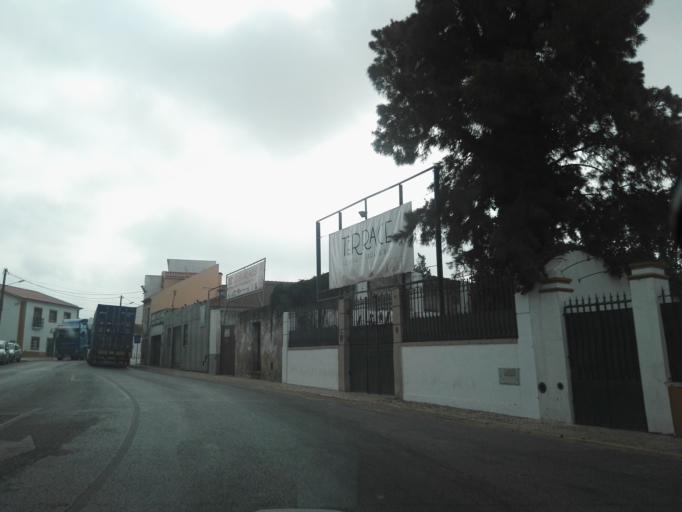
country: PT
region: Santarem
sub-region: Benavente
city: Benavente
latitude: 38.9837
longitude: -8.8089
